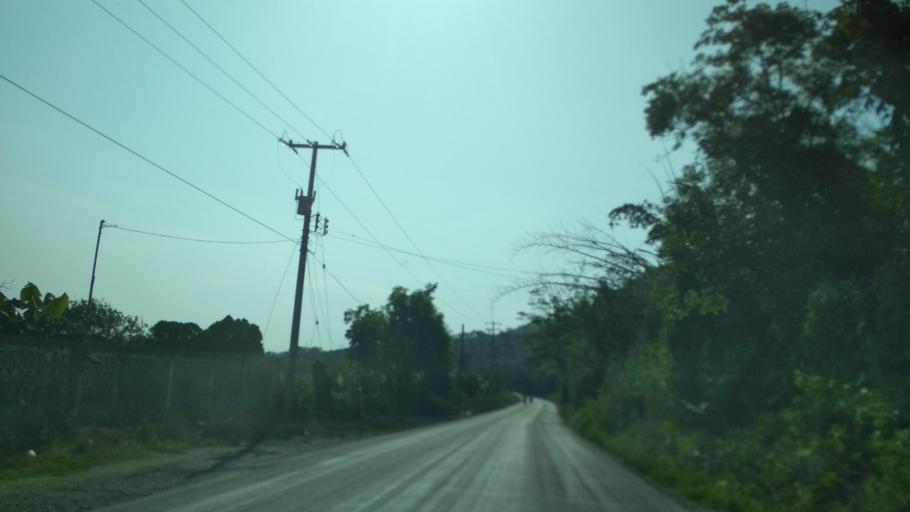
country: MX
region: Veracruz
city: Agua Dulce
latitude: 20.3938
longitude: -97.2762
